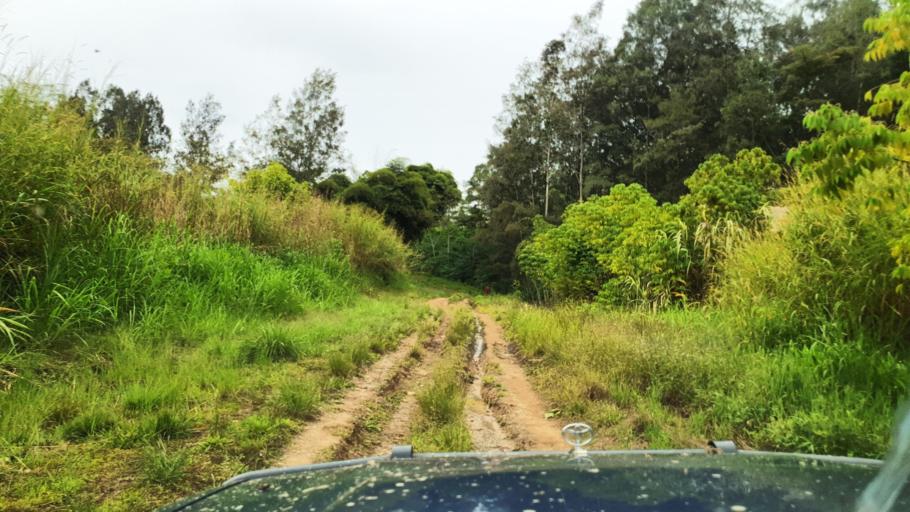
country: PG
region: Jiwaka
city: Minj
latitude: -5.9319
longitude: 144.7513
